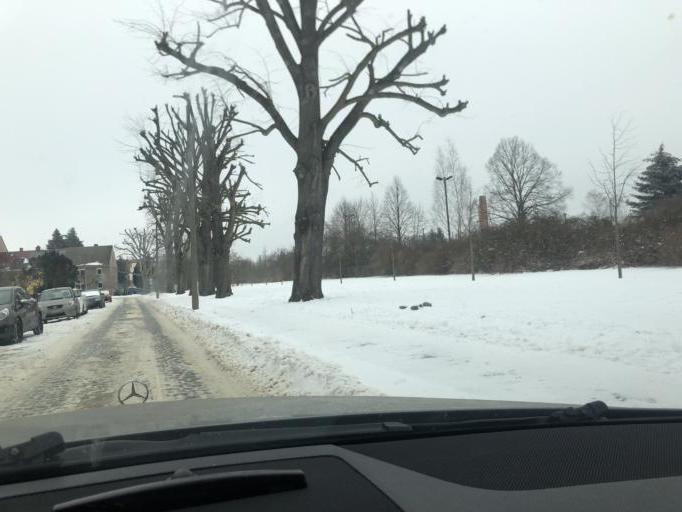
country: DE
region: Brandenburg
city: Guben
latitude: 51.9492
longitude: 14.7089
